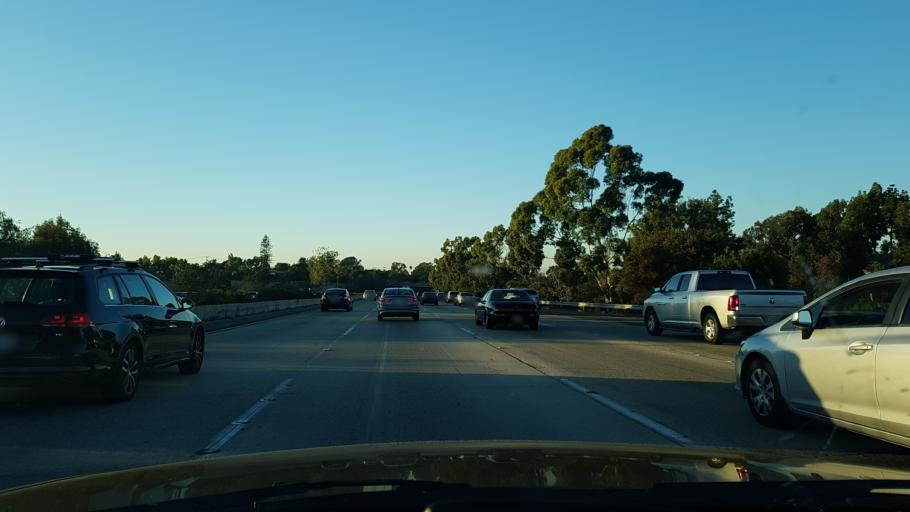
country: US
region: California
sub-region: San Diego County
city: Encinitas
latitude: 33.0390
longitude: -117.2832
